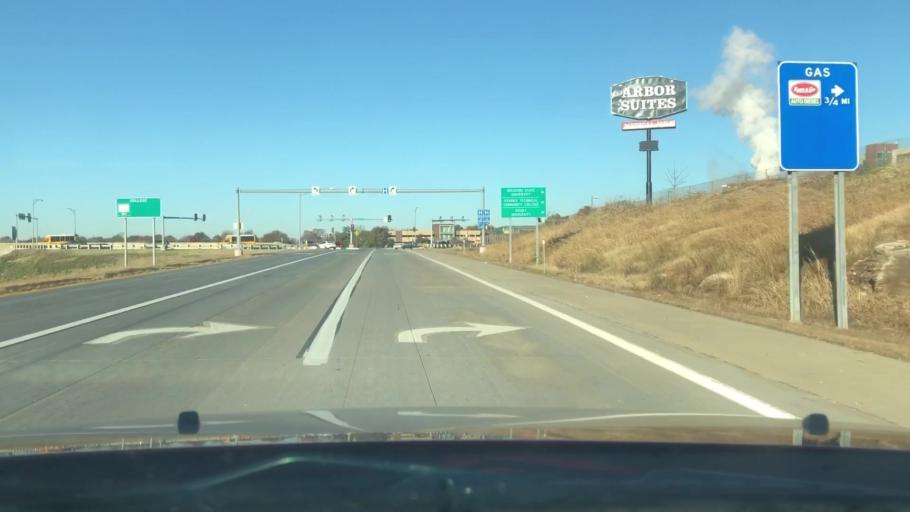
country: US
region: Missouri
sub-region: Greene County
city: Springfield
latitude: 37.1427
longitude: -93.2762
